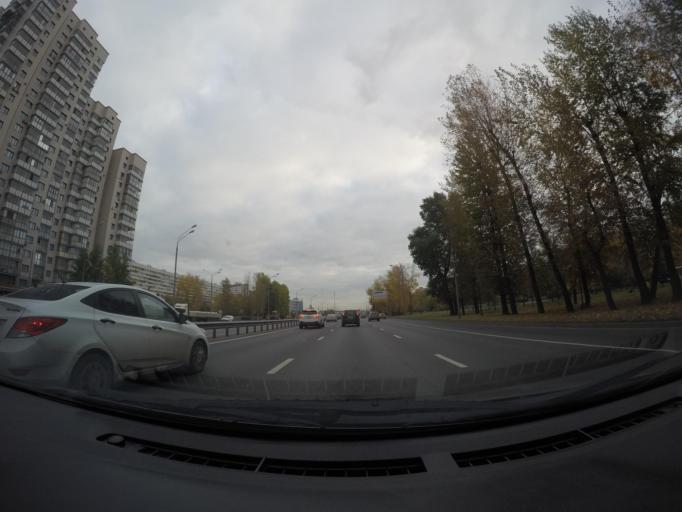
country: RU
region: Moscow
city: Ivanovskoye
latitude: 55.7739
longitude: 37.8300
